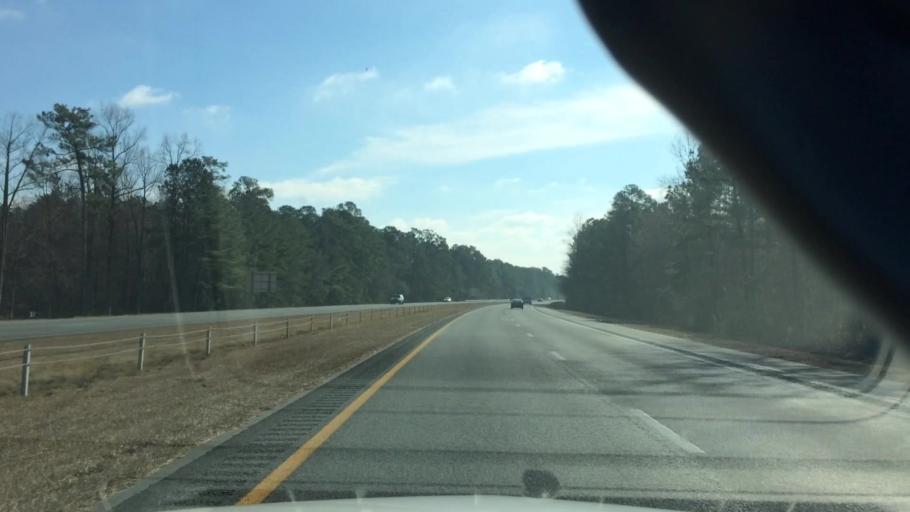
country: US
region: North Carolina
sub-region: Duplin County
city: Wallace
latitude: 34.7490
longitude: -77.9461
